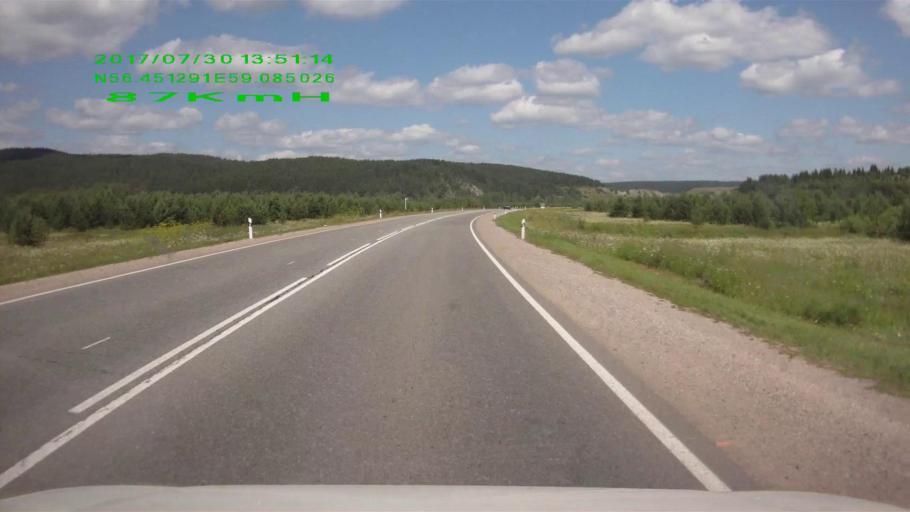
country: RU
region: Sverdlovsk
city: Mikhaylovsk
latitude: 56.4518
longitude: 59.0854
